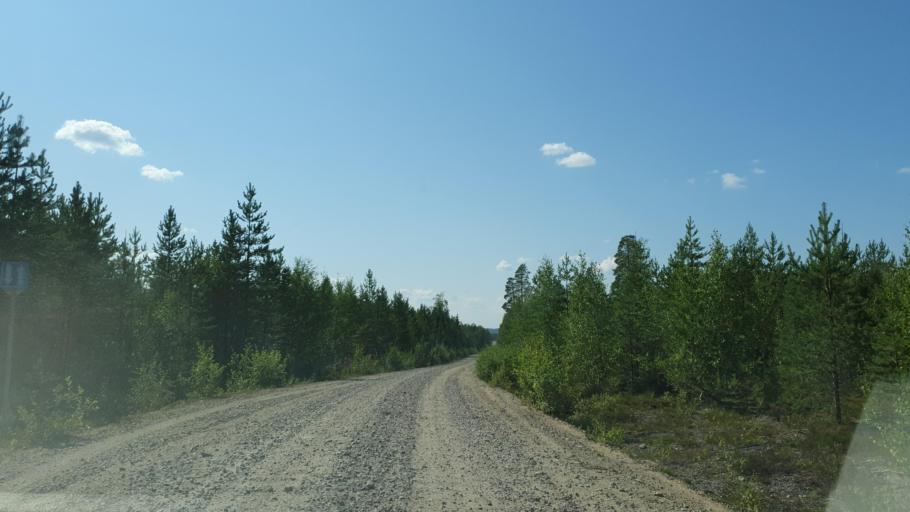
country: FI
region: Kainuu
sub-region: Kehys-Kainuu
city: Kuhmo
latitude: 64.0111
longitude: 29.5900
